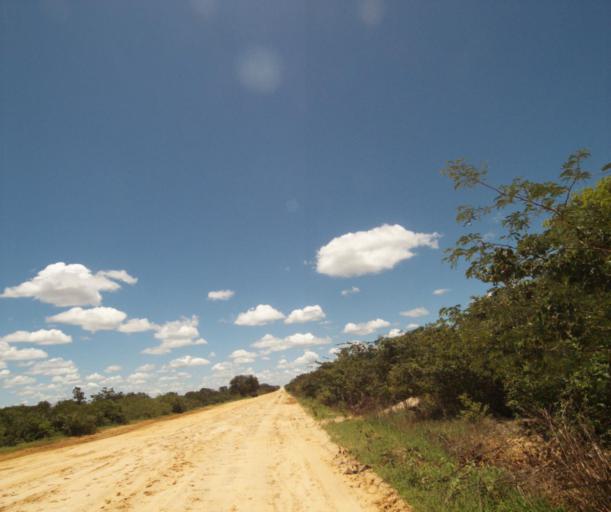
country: BR
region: Bahia
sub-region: Carinhanha
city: Carinhanha
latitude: -14.2767
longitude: -43.7989
